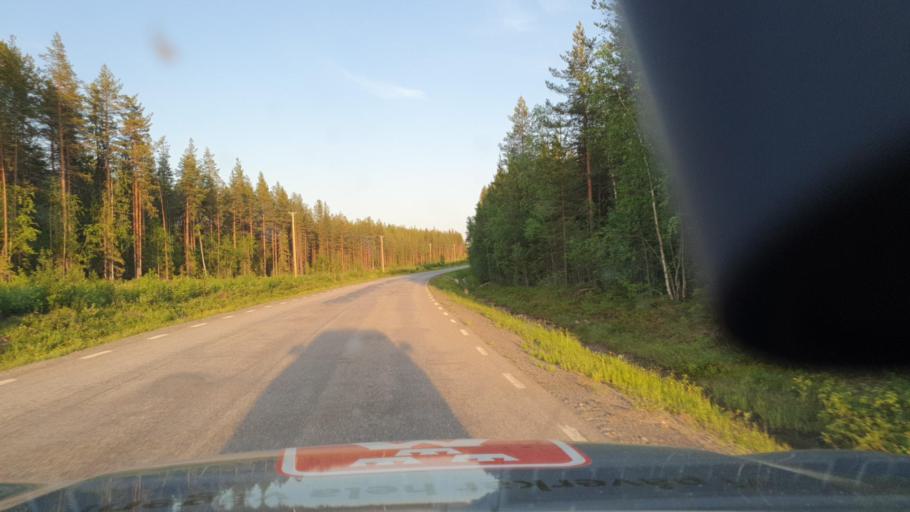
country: SE
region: Norrbotten
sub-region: Bodens Kommun
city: Boden
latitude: 66.0123
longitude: 21.8387
